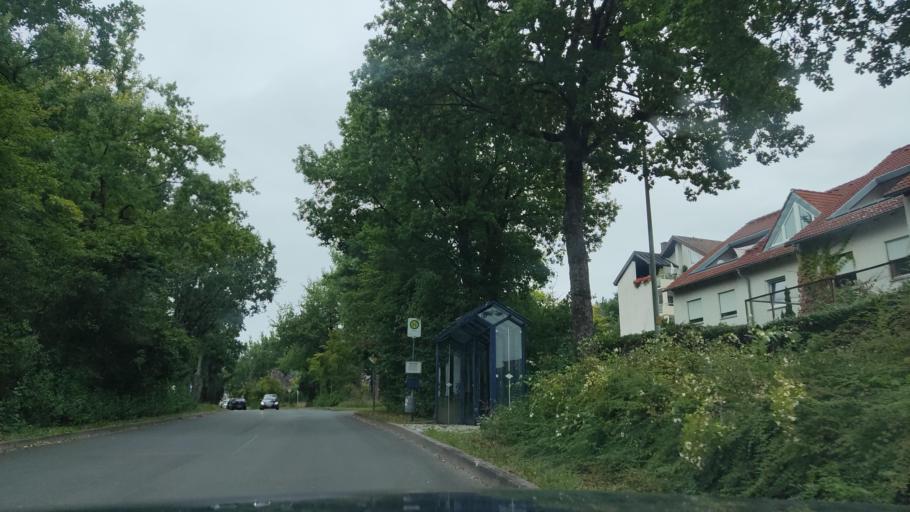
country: DE
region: Bavaria
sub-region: Upper Franconia
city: Kronach
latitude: 50.2373
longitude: 11.3469
